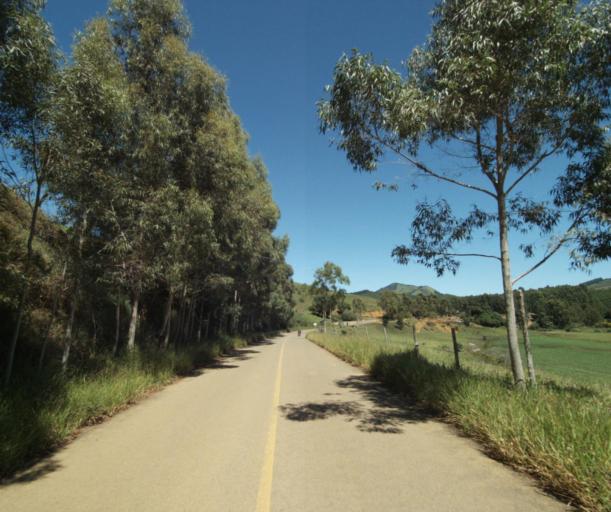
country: BR
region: Minas Gerais
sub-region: Espera Feliz
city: Espera Feliz
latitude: -20.5775
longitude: -41.8331
